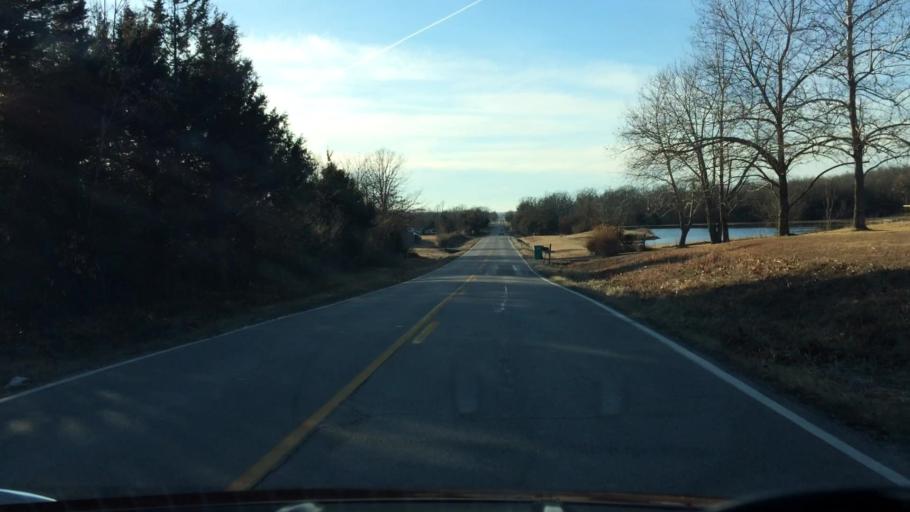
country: US
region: Missouri
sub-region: Webster County
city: Marshfield
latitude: 37.3409
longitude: -92.9806
